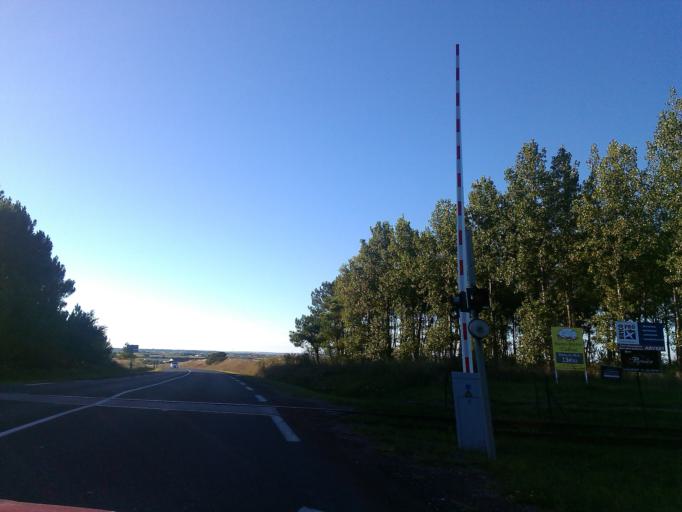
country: FR
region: Poitou-Charentes
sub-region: Departement de la Charente-Maritime
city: Etaules
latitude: 45.7357
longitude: -1.0832
